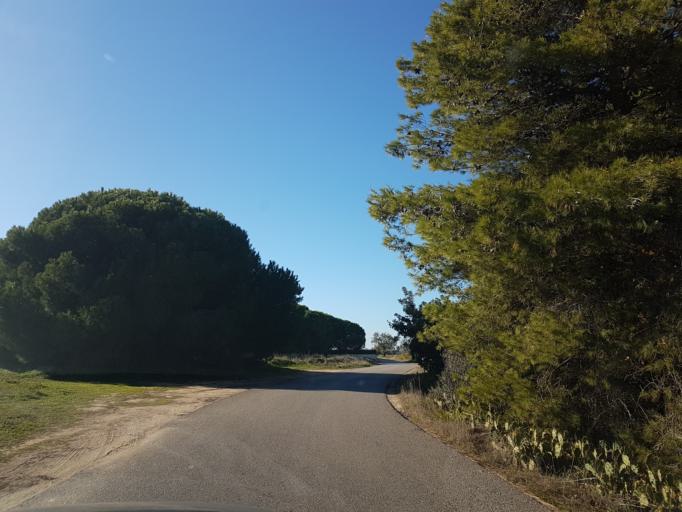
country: PT
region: Faro
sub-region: Silves
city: Armacao de Pera
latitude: 37.1189
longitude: -8.4028
